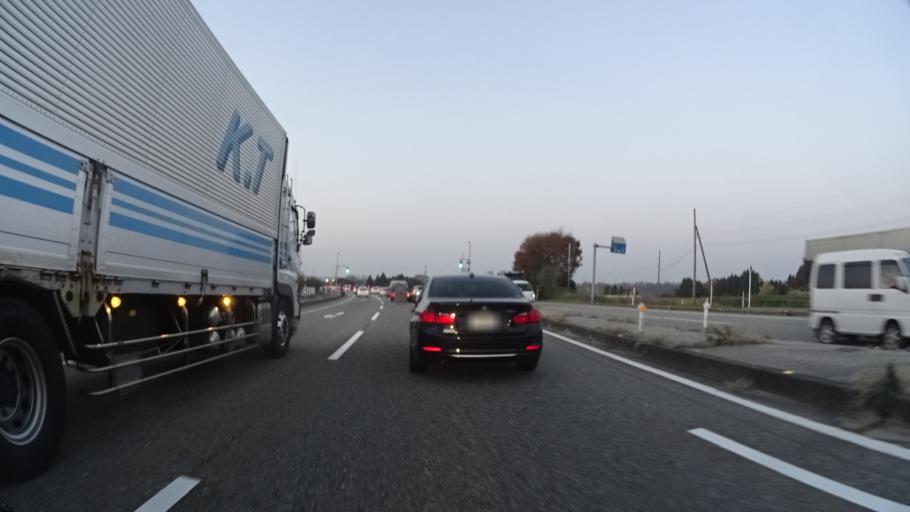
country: JP
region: Toyama
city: Uozu
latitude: 36.7911
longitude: 137.4073
